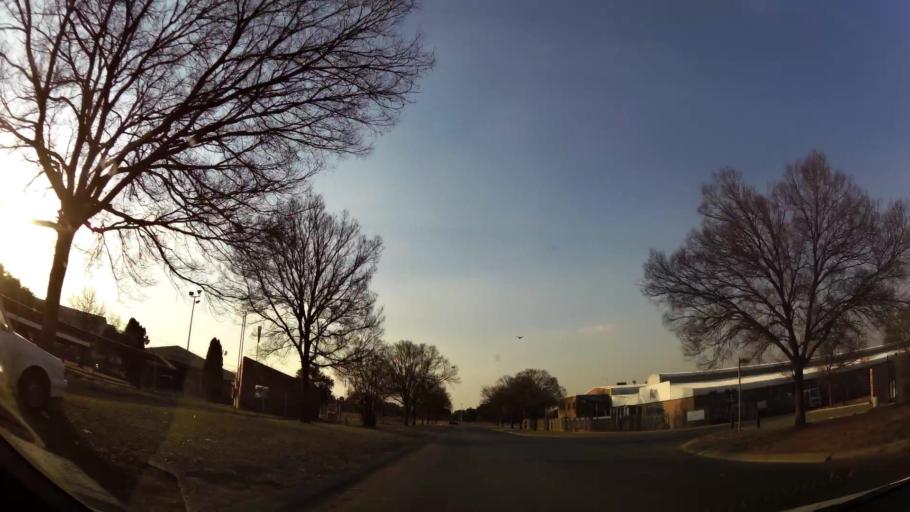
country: ZA
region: Gauteng
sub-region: Ekurhuleni Metropolitan Municipality
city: Springs
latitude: -26.2549
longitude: 28.4081
